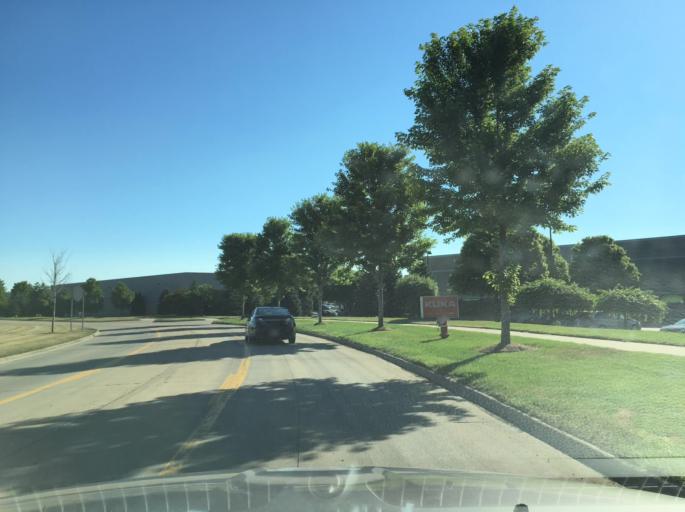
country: US
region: Michigan
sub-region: Macomb County
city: Shelby
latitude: 42.6759
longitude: -83.0129
